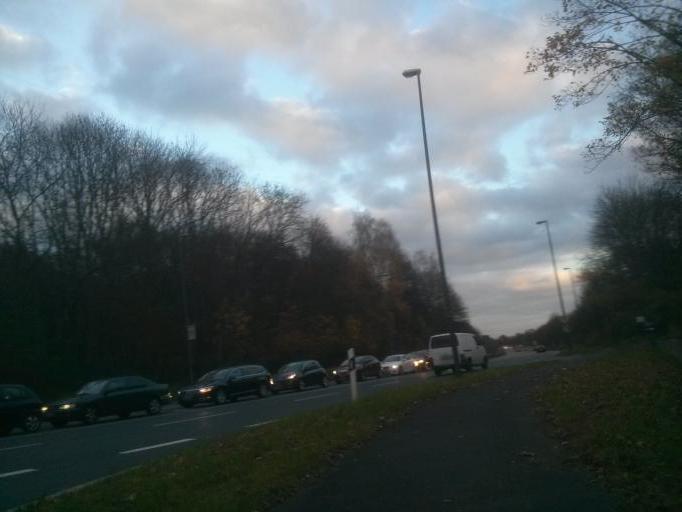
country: DE
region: North Rhine-Westphalia
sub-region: Regierungsbezirk Koln
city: Poll
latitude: 50.9092
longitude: 7.0042
